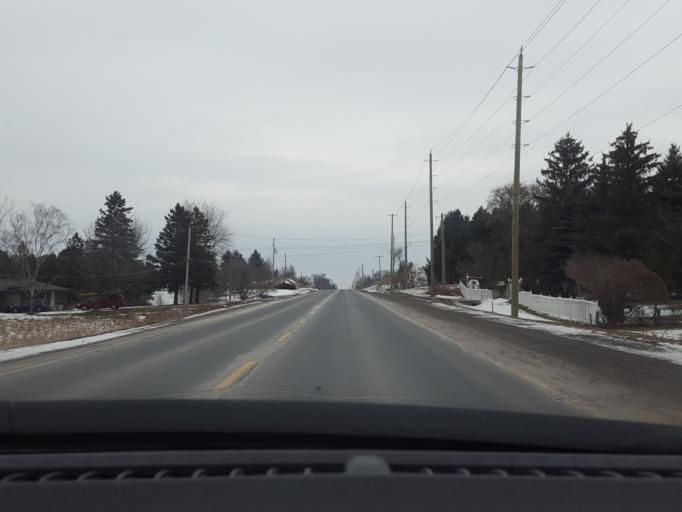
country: CA
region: Ontario
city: Keswick
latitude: 44.1685
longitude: -79.4322
